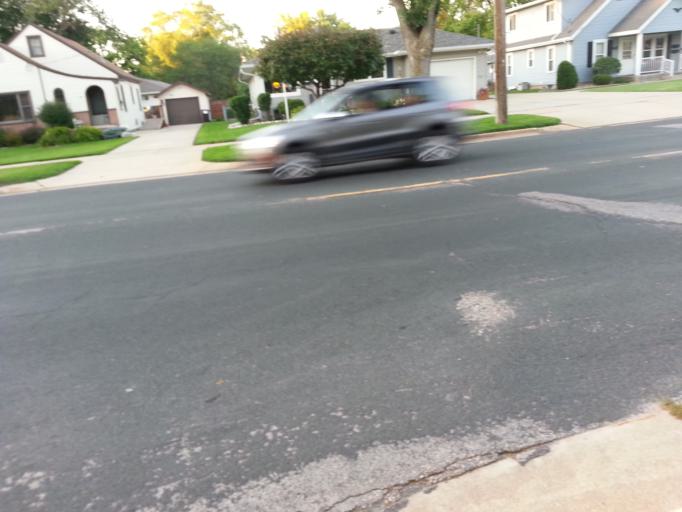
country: US
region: Minnesota
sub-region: Olmsted County
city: Rochester
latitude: 44.0361
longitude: -92.4564
